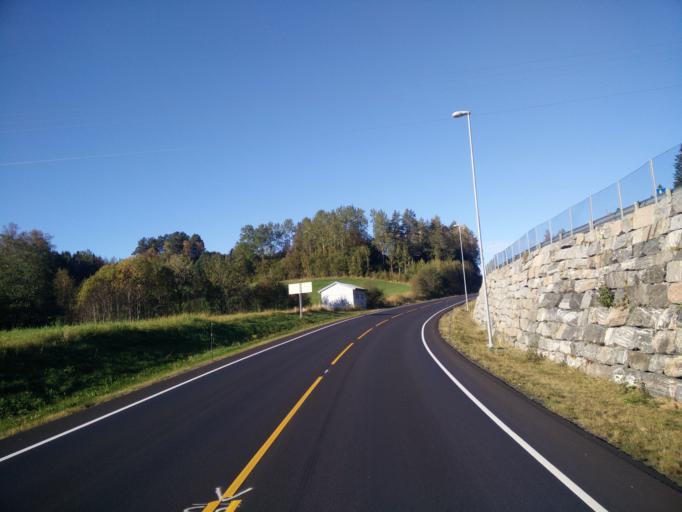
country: NO
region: More og Romsdal
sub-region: Halsa
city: Liaboen
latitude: 63.0891
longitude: 8.3529
